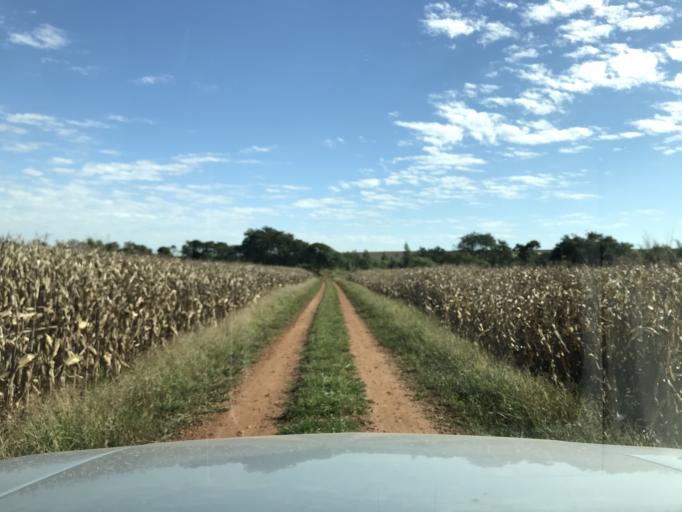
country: BR
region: Parana
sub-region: Ipora
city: Ipora
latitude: -24.1522
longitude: -53.7457
